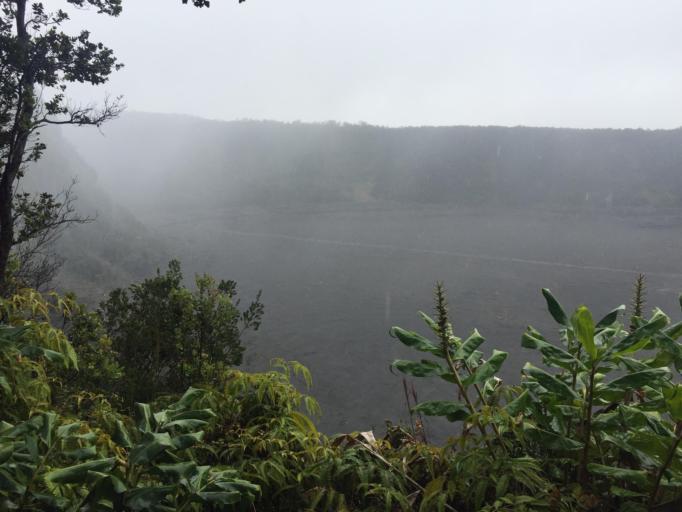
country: US
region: Hawaii
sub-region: Hawaii County
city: Volcano
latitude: 19.4174
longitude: -155.2452
